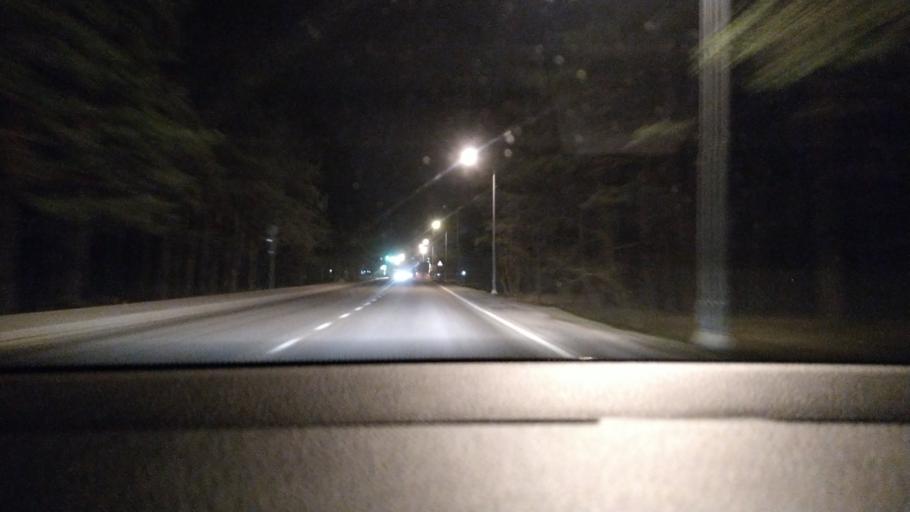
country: RU
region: Moskovskaya
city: Selyatino
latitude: 55.4833
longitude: 36.9146
